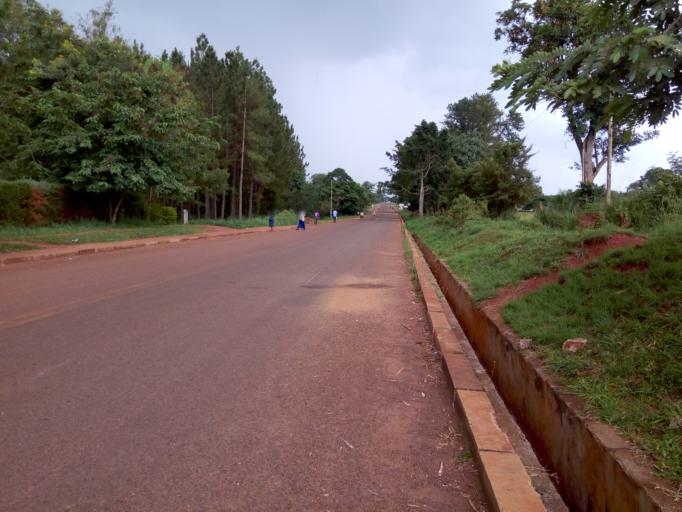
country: UG
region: Western Region
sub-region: Masindi District
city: Masindi
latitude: 1.6834
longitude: 31.7040
